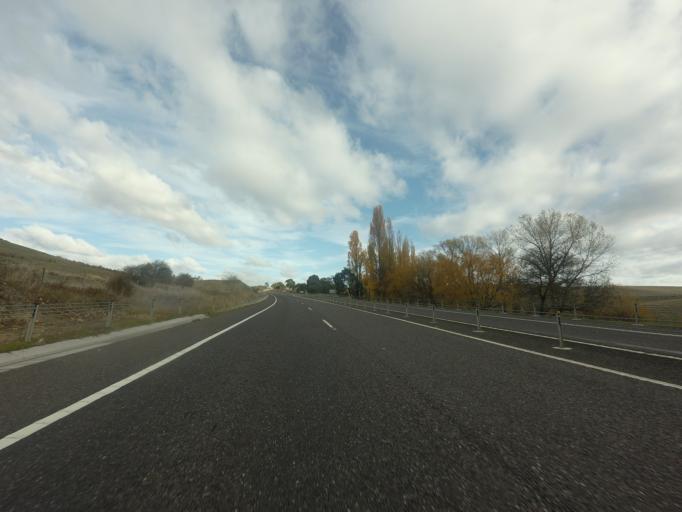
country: AU
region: Tasmania
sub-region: Brighton
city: Bridgewater
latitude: -42.5629
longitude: 147.2085
